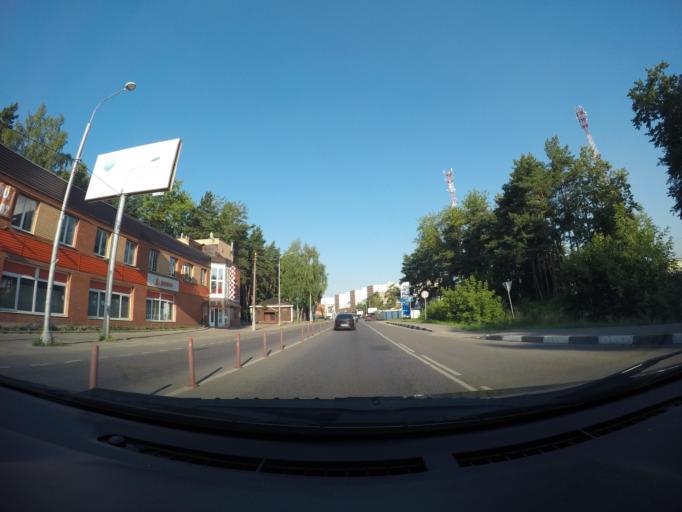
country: RU
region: Moskovskaya
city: Korenevo
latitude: 55.6629
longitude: 38.0067
